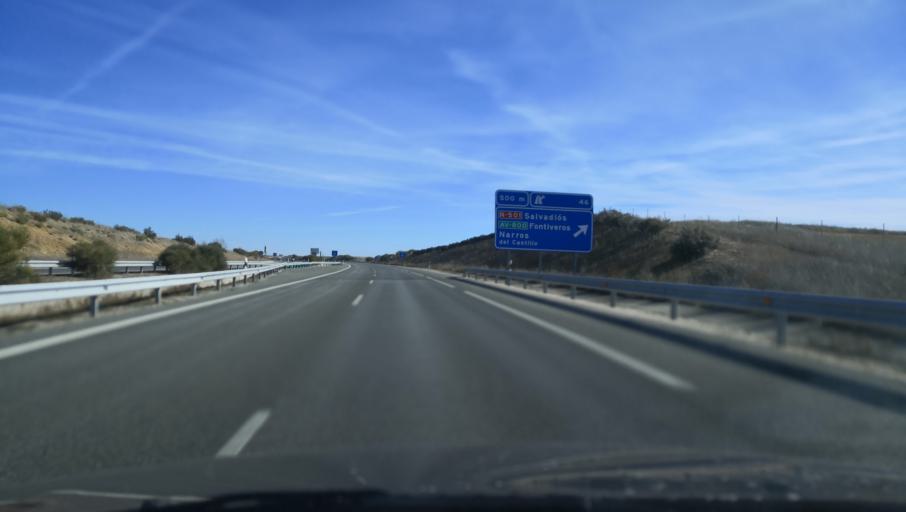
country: ES
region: Castille and Leon
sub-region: Provincia de Avila
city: Narros del Castillo
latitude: 40.8736
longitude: -5.0681
